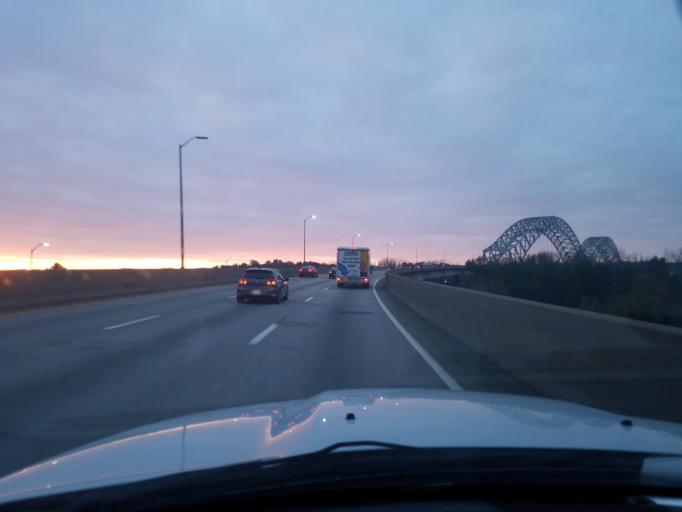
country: US
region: Indiana
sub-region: Floyd County
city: New Albany
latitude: 38.2754
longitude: -85.8169
